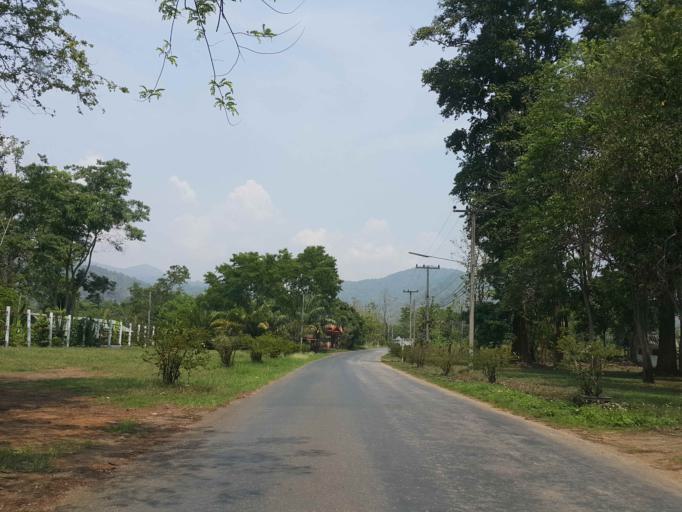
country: TH
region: Chiang Mai
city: Mae Taeng
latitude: 19.1431
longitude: 98.8661
